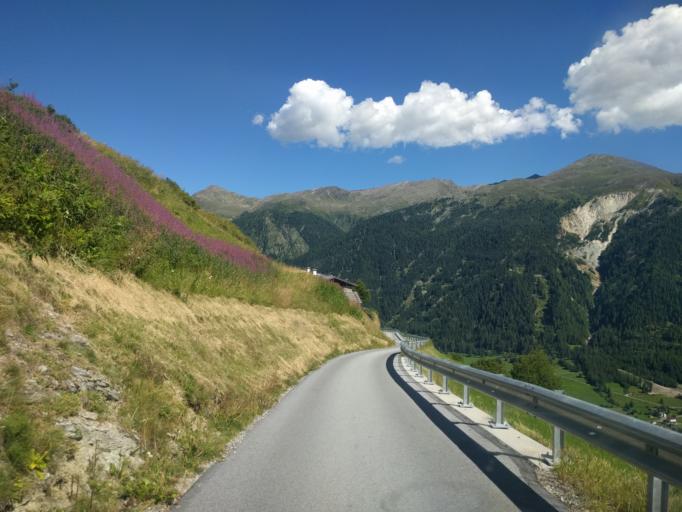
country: IT
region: Trentino-Alto Adige
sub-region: Bolzano
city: Tubre
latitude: 46.6089
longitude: 10.4085
